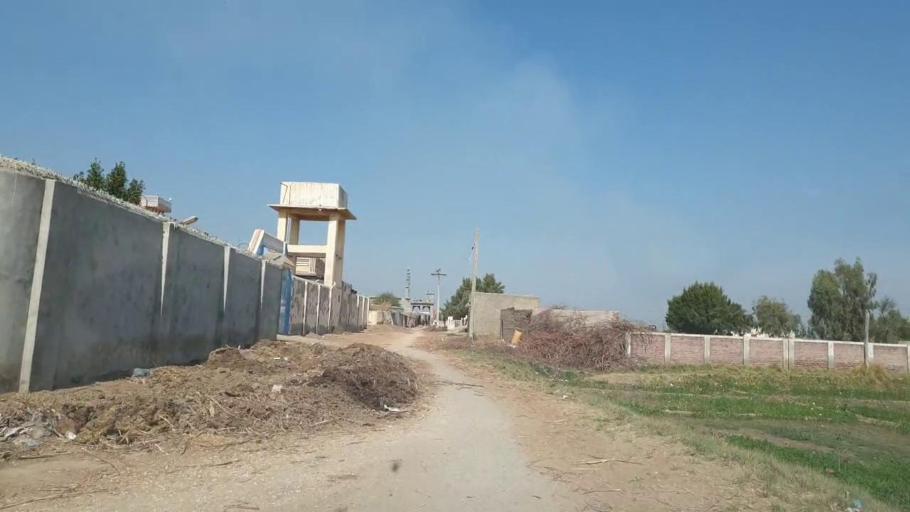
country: PK
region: Sindh
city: Mirpur Khas
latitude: 25.7360
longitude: 69.0972
